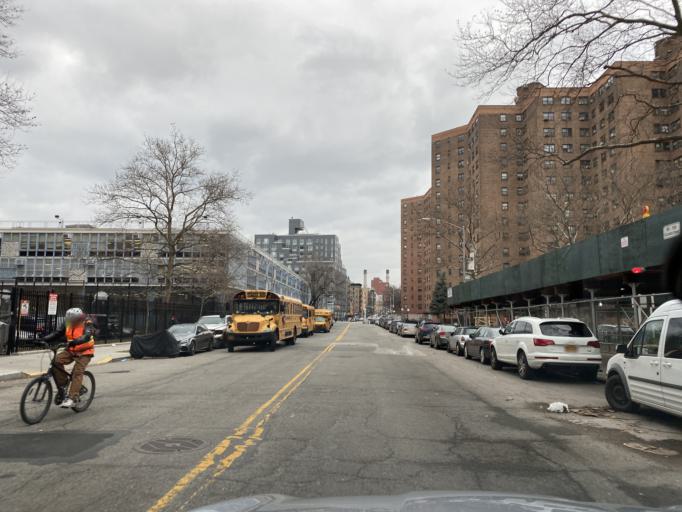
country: US
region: New York
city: New York City
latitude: 40.7183
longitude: -73.9796
